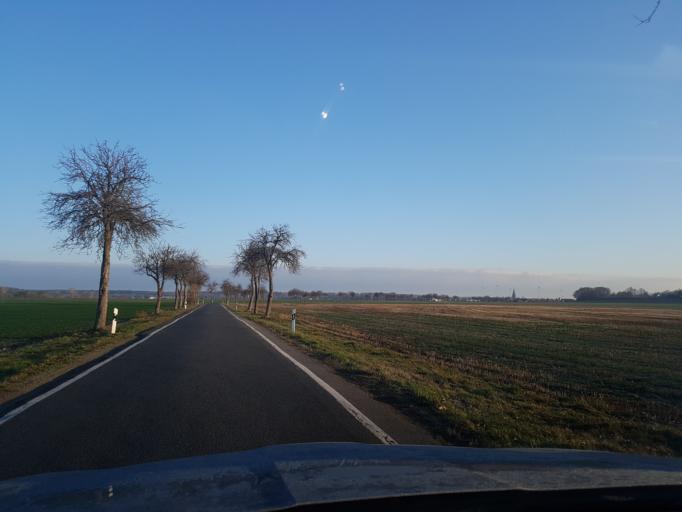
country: DE
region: Brandenburg
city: Schlieben
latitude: 51.7162
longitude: 13.3614
